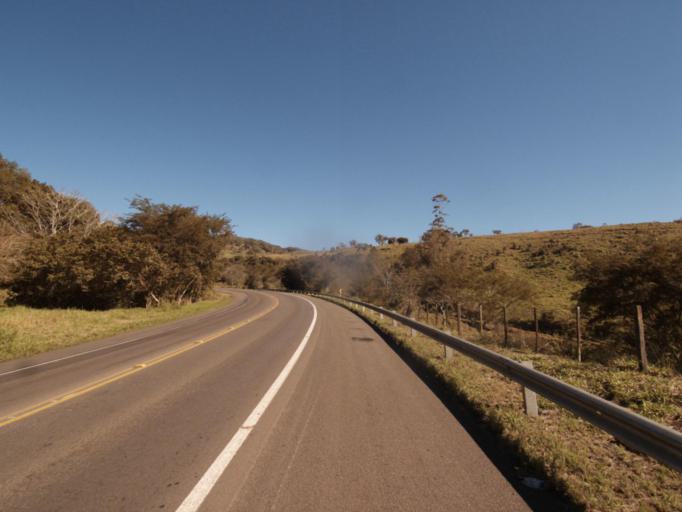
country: BR
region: Rio Grande do Sul
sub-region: Frederico Westphalen
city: Frederico Westphalen
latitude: -26.8228
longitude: -53.4114
